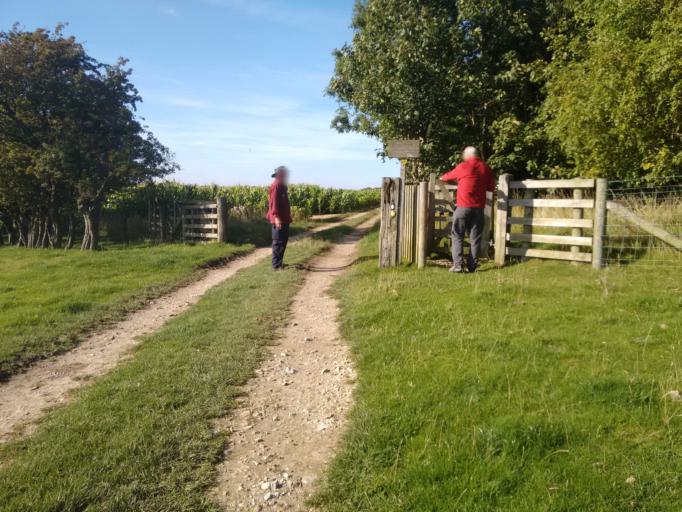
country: GB
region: England
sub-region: North Yorkshire
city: Thixendale
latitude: 54.0432
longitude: -0.7225
